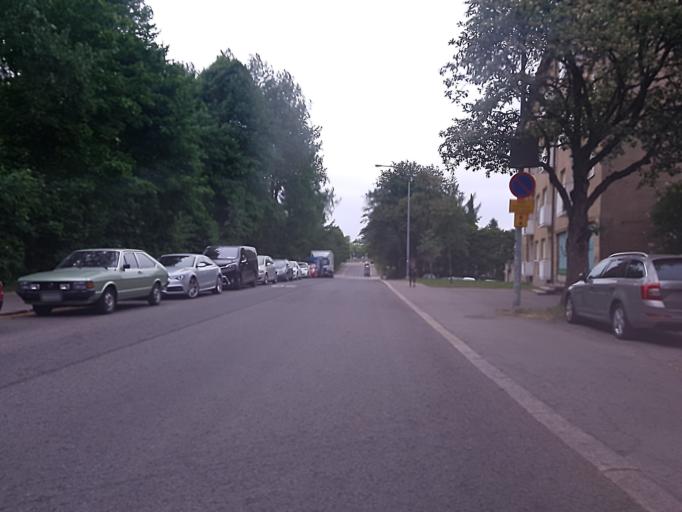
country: FI
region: Uusimaa
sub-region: Helsinki
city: Helsinki
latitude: 60.2057
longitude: 24.9487
